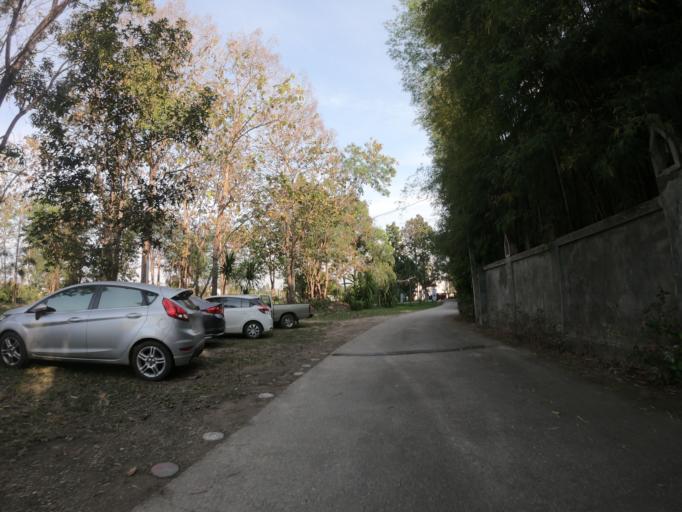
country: TH
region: Chiang Mai
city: Chiang Mai
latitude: 18.8273
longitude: 98.9546
